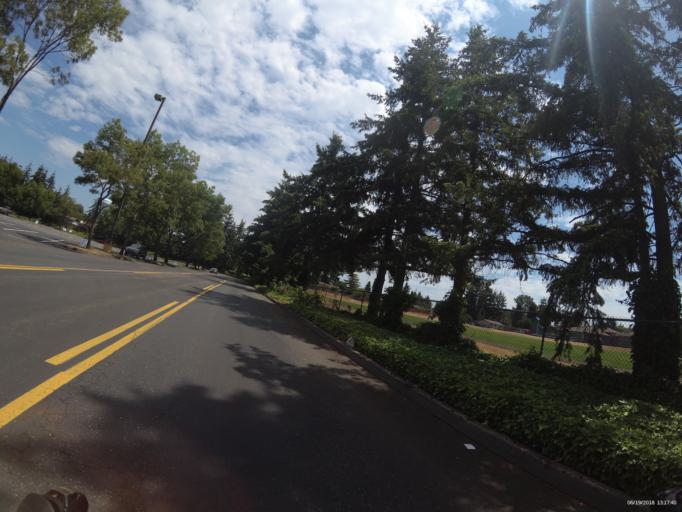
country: US
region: Washington
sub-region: Pierce County
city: Lakewood
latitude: 47.1611
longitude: -122.5116
